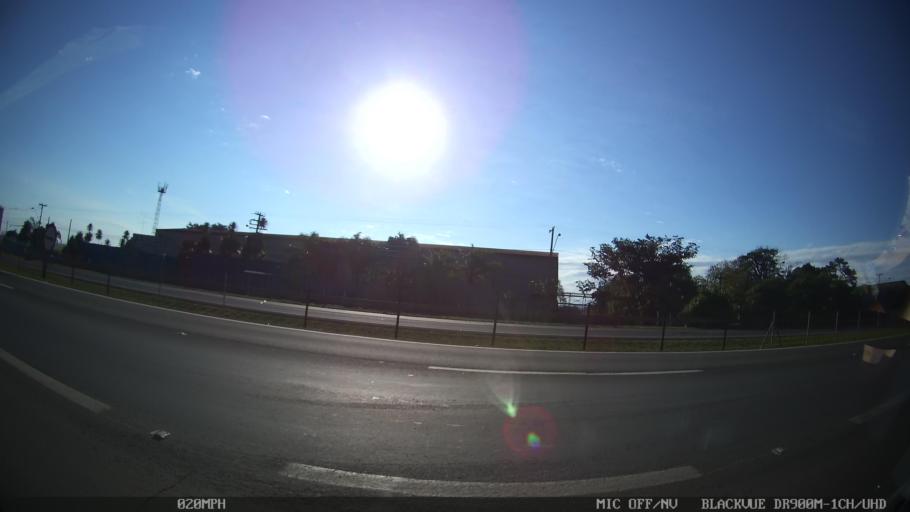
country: BR
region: Sao Paulo
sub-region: Piracicaba
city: Piracicaba
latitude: -22.6718
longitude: -47.6277
